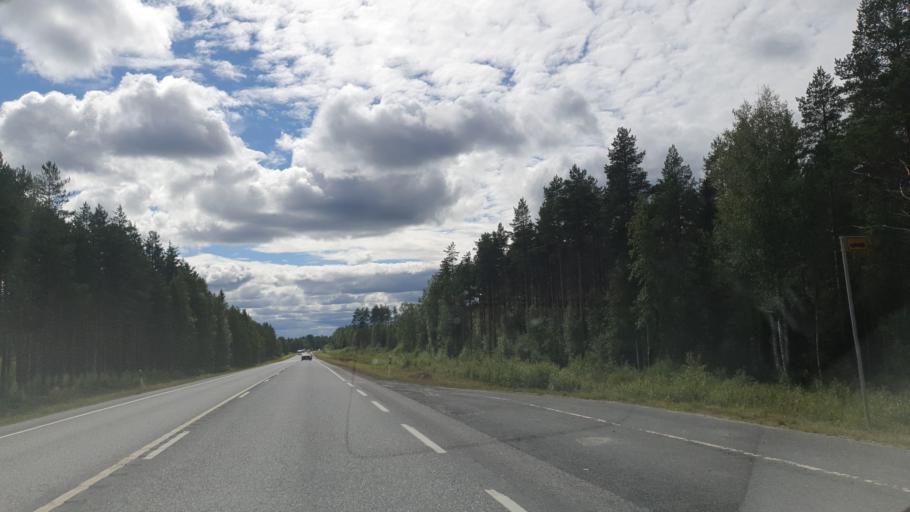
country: FI
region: Kainuu
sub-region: Kajaani
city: Kajaani
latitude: 64.1283
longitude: 27.4745
